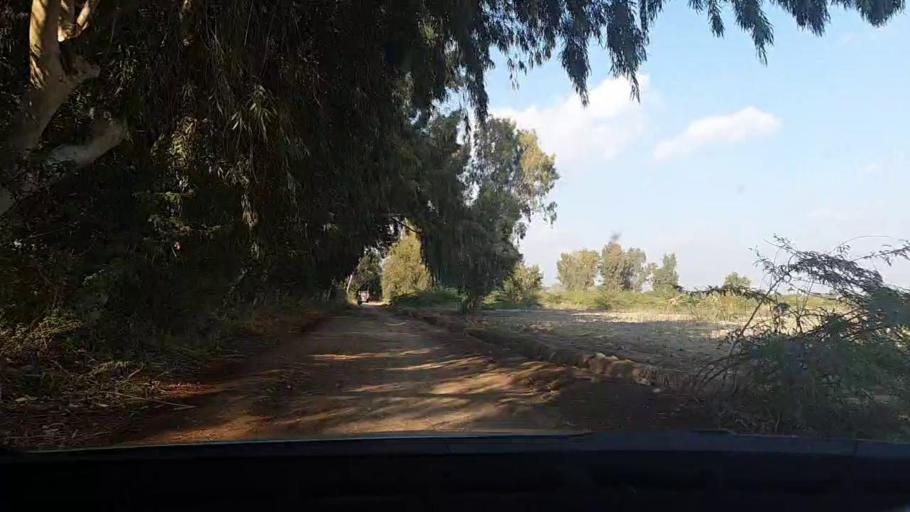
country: PK
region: Sindh
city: Tando Mittha Khan
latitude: 25.8929
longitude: 69.2979
